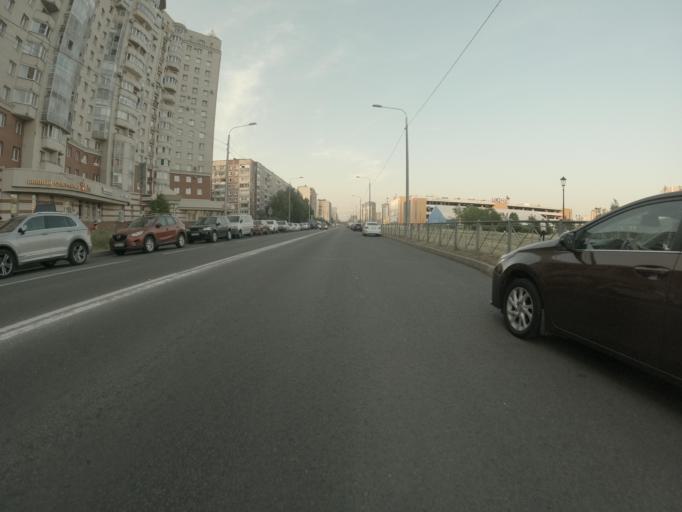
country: RU
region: St.-Petersburg
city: Krasnogvargeisky
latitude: 59.9460
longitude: 30.4689
